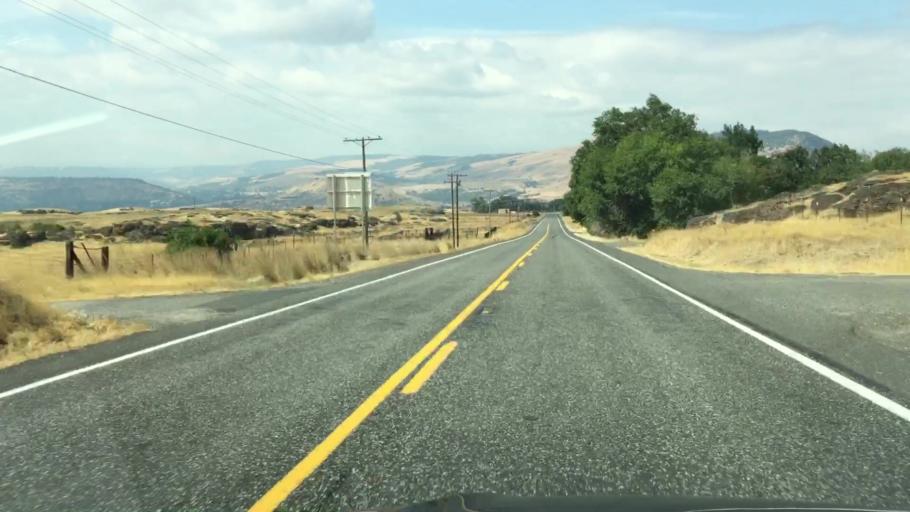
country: US
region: Washington
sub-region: Klickitat County
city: Dallesport
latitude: 45.6487
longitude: -121.1671
